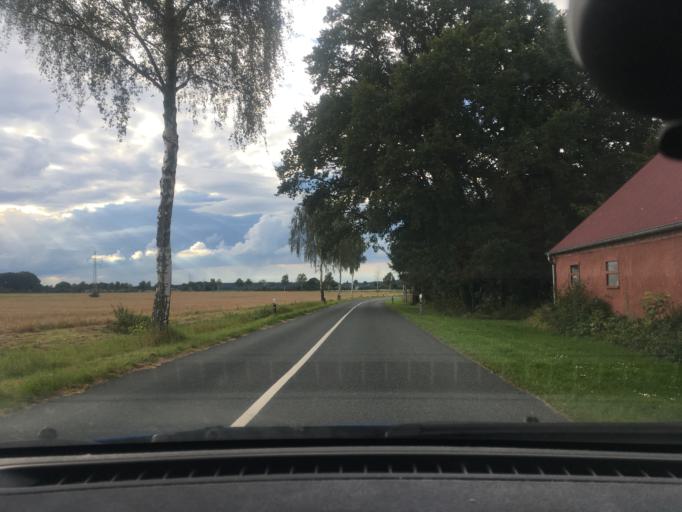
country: DE
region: Lower Saxony
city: Nahrendorf
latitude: 53.1613
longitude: 10.8291
